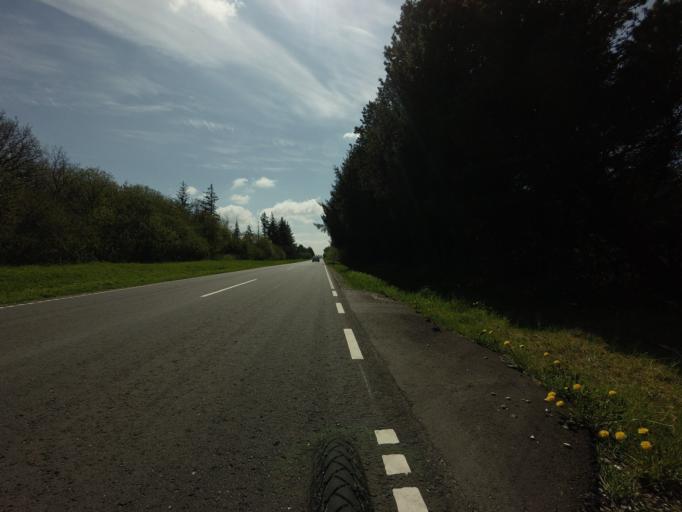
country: DK
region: North Denmark
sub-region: Jammerbugt Kommune
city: Brovst
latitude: 57.1584
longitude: 9.5759
